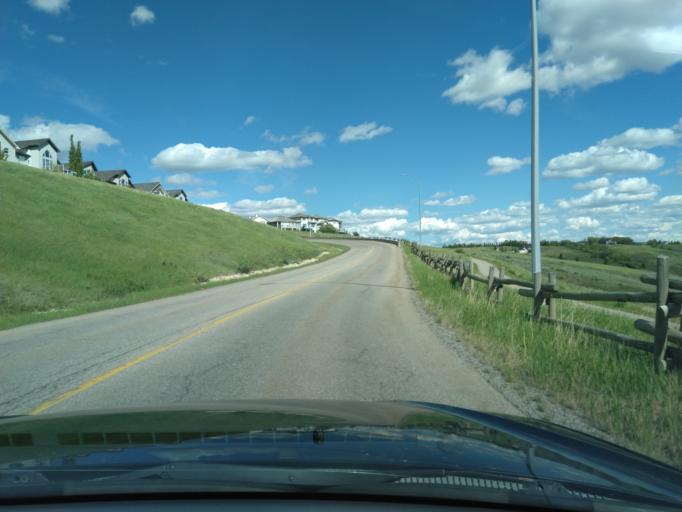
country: CA
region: Alberta
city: Cochrane
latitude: 51.1950
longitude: -114.4256
